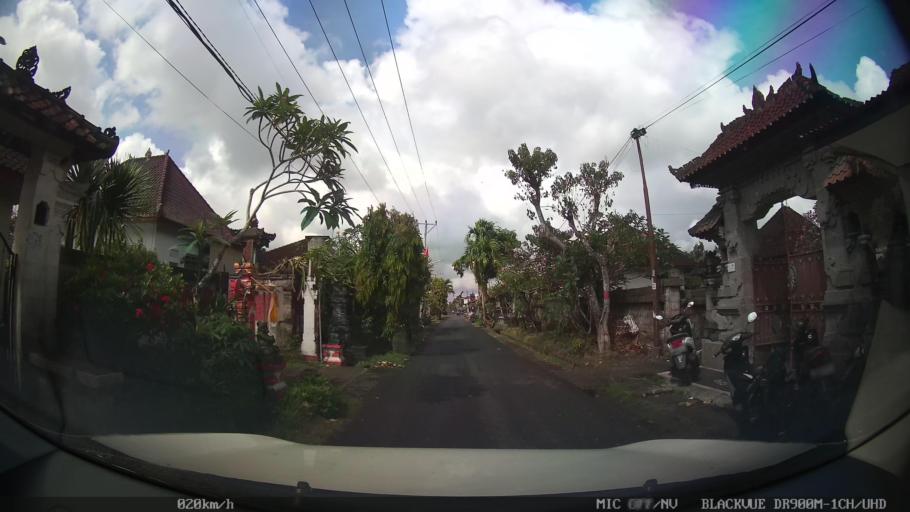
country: ID
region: Bali
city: Banjar Karangsuling
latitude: -8.5951
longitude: 115.1980
